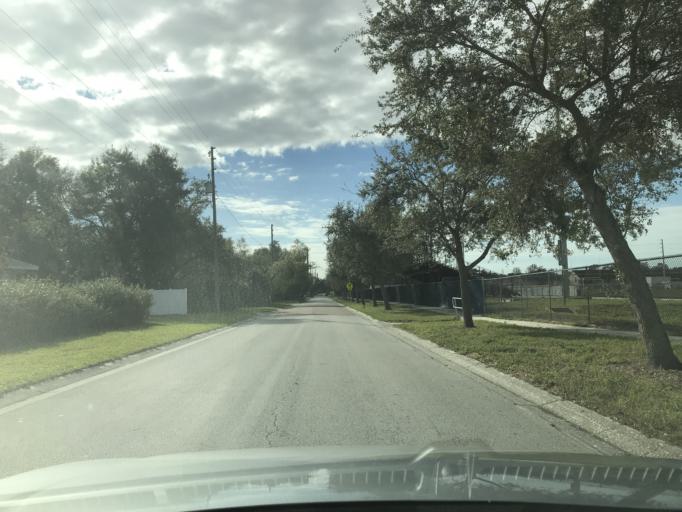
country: US
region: Florida
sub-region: Pinellas County
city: Largo
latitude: 27.9203
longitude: -82.7834
